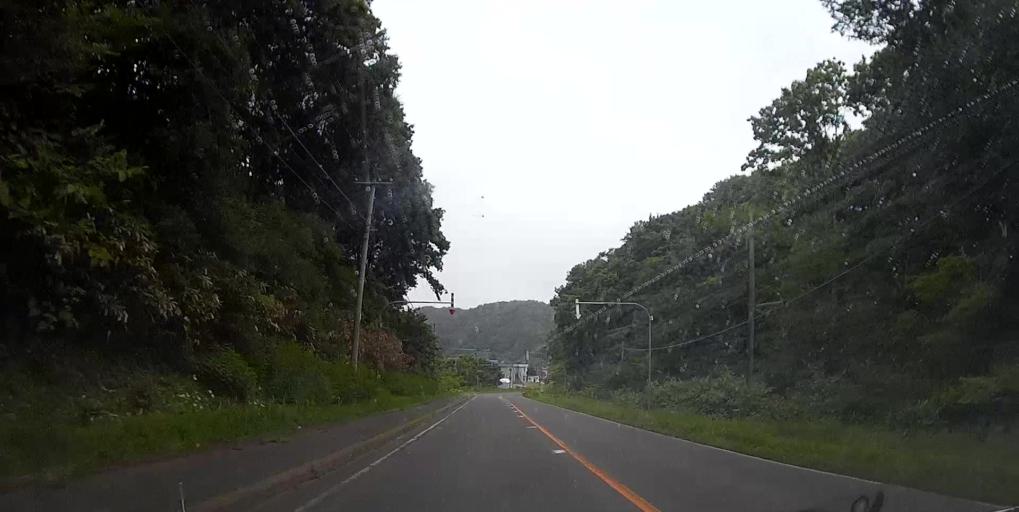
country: JP
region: Hokkaido
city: Iwanai
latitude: 42.4347
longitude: 139.9963
